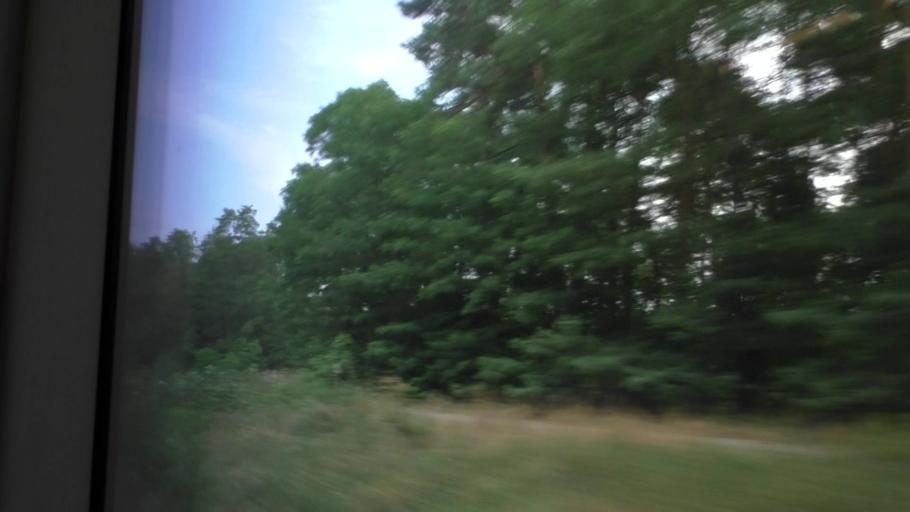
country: DE
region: Brandenburg
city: Mullrose
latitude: 52.2310
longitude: 14.4297
